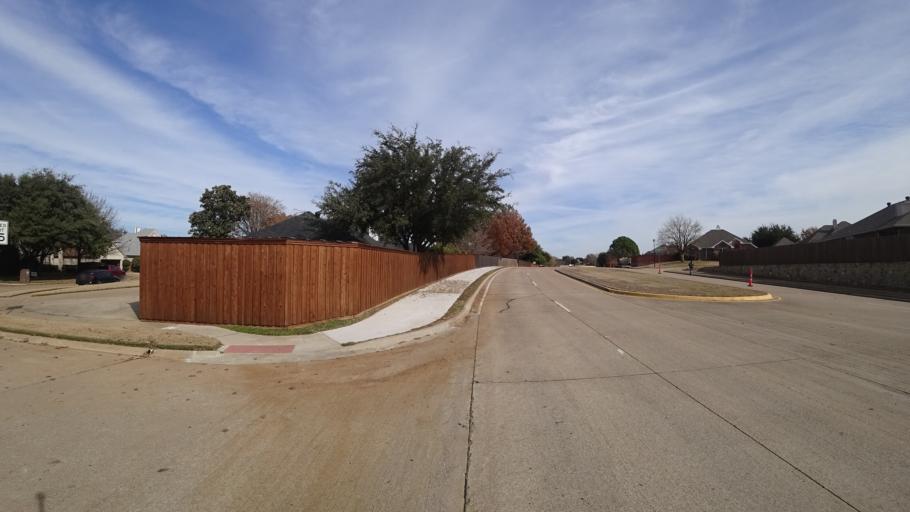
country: US
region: Texas
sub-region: Denton County
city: Highland Village
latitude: 33.0824
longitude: -97.0346
